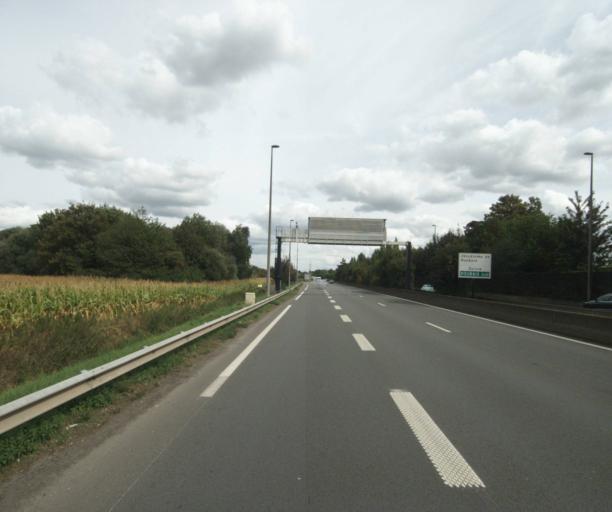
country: FR
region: Nord-Pas-de-Calais
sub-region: Departement du Nord
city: Wasquehal
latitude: 50.6475
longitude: 3.1539
